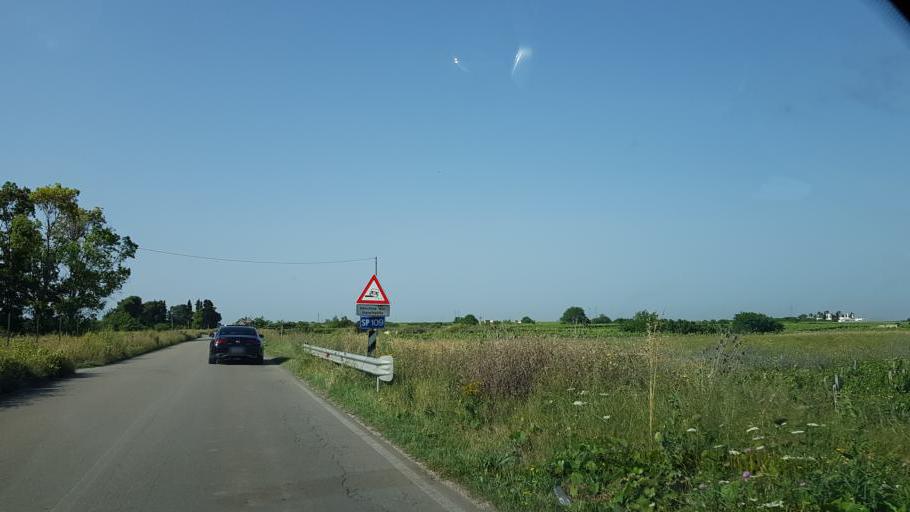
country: IT
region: Apulia
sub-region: Provincia di Brindisi
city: San Pancrazio Salentino
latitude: 40.4064
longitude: 17.8361
